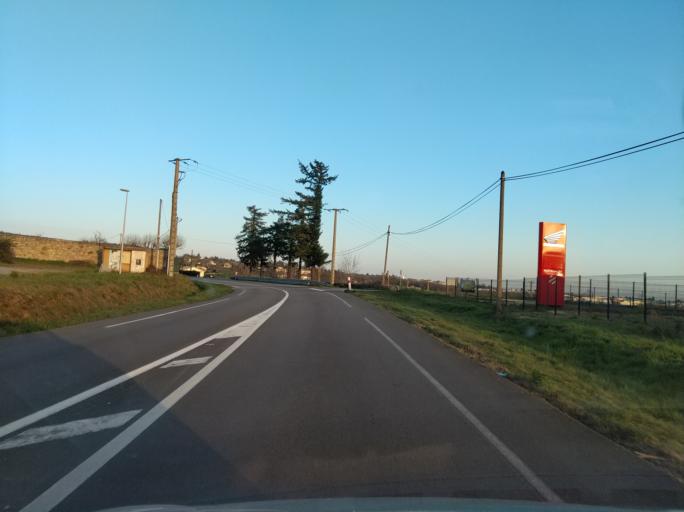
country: FR
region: Rhone-Alpes
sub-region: Departement de l'Ardeche
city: Boulieu-les-Annonay
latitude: 45.2684
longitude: 4.6823
